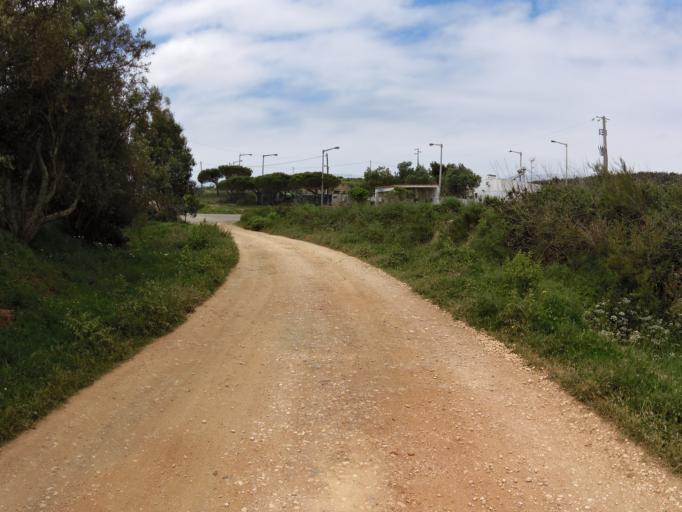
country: PT
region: Faro
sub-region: Vila do Bispo
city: Vila do Bispo
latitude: 37.0884
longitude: -8.9022
